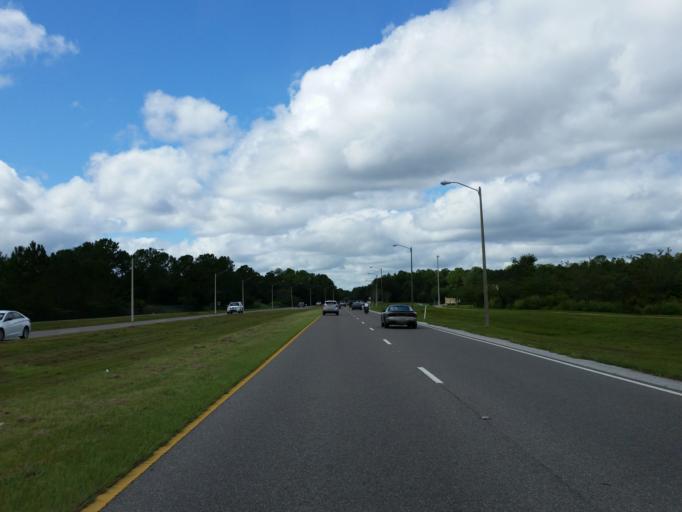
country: US
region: Florida
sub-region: Hillsborough County
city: Pebble Creek
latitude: 28.1422
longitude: -82.3348
